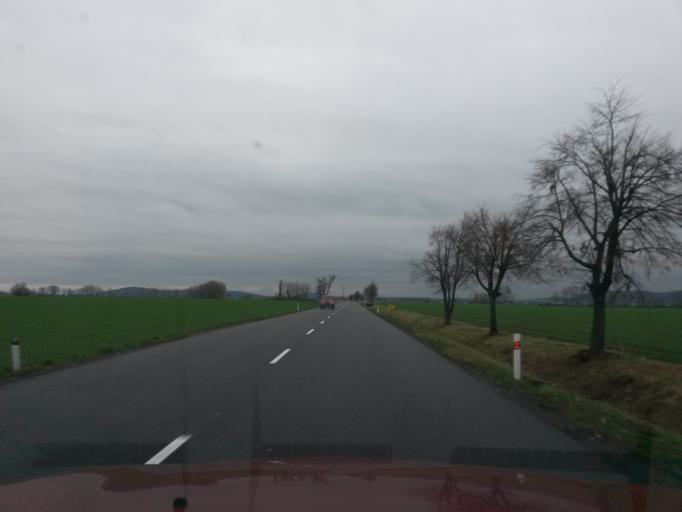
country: SK
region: Kosicky
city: Trebisov
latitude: 48.5526
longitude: 21.6818
